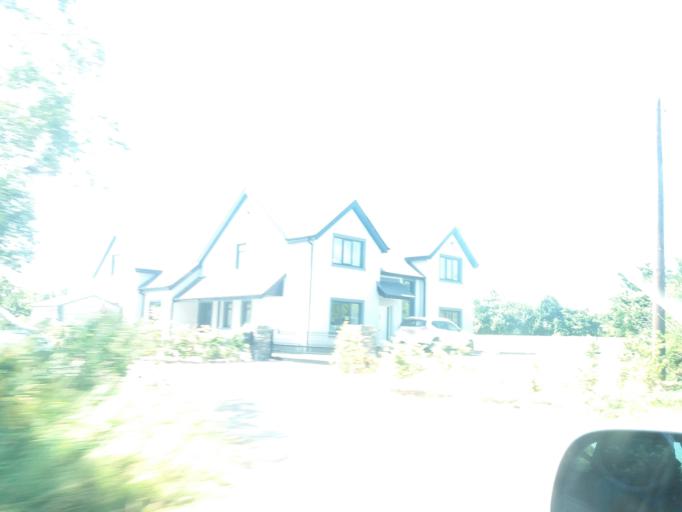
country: IE
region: Leinster
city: Balrothery
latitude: 53.5394
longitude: -6.2388
